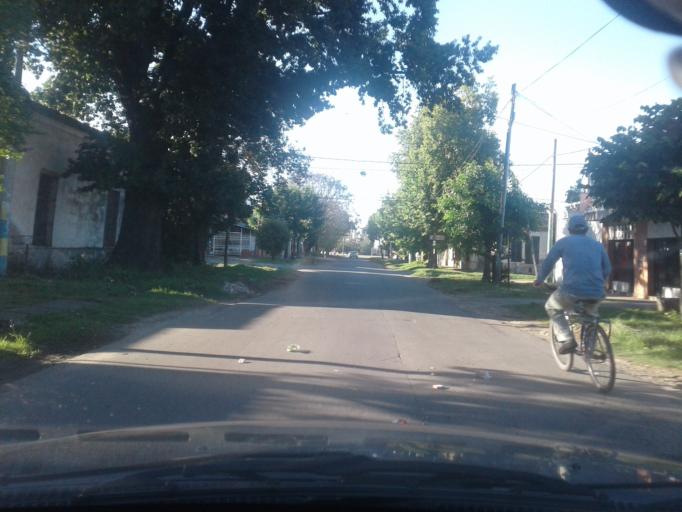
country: AR
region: Santa Fe
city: Granadero Baigorria
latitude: -32.8886
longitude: -60.7241
